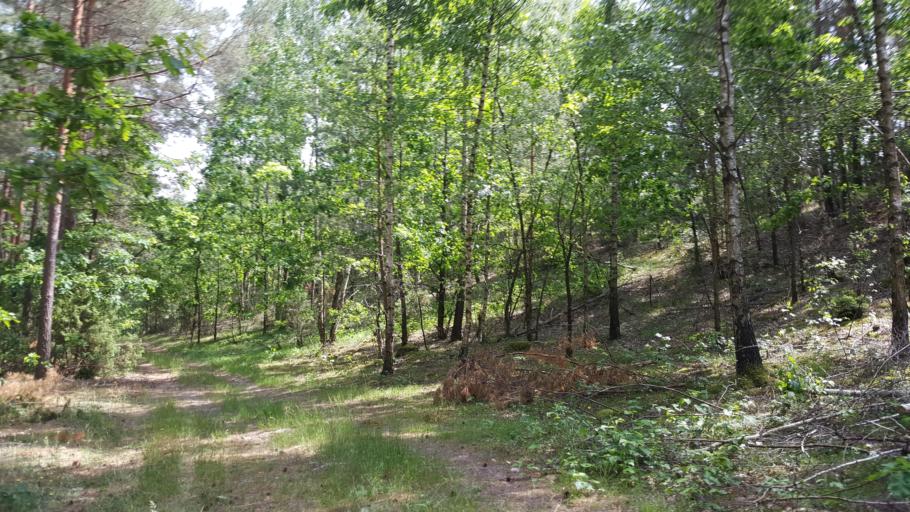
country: BY
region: Brest
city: Kamyanyuki
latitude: 52.5056
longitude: 23.8293
